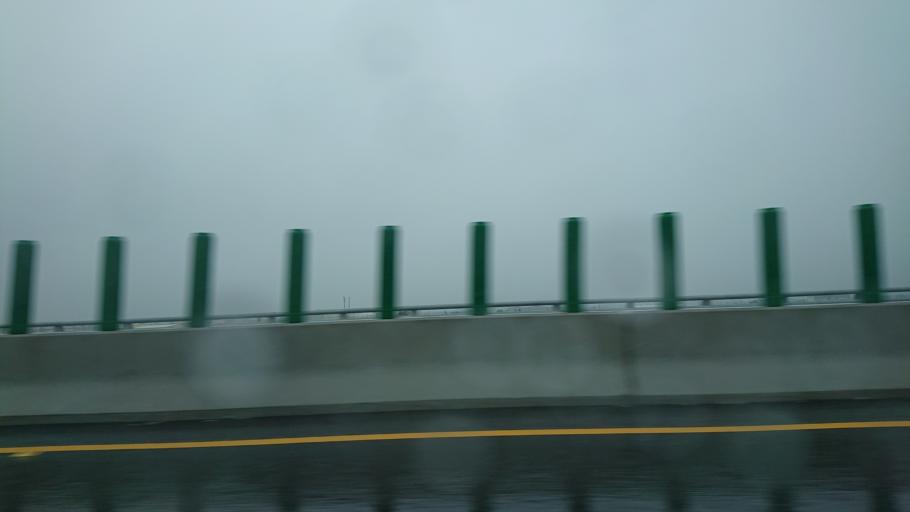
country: TW
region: Taiwan
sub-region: Changhua
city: Chang-hua
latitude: 23.9200
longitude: 120.3117
